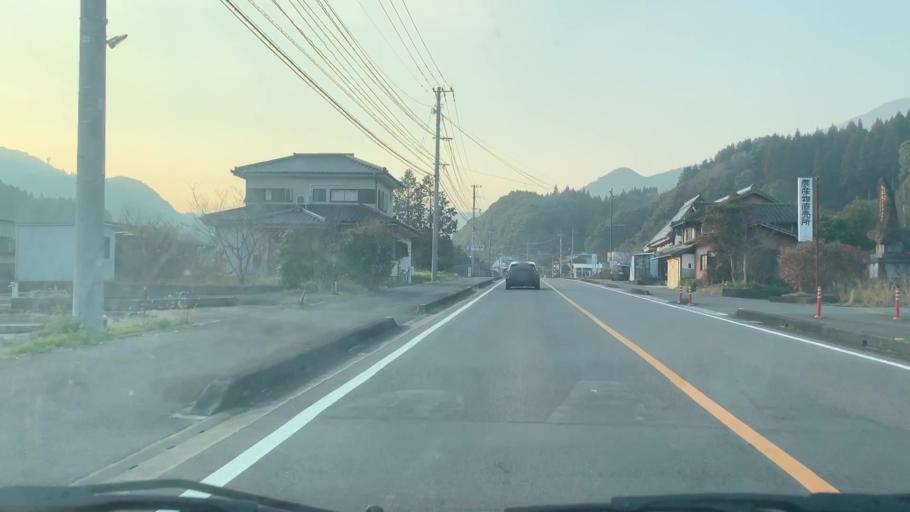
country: JP
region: Saga Prefecture
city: Takeocho-takeo
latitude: 33.2635
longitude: 130.0548
